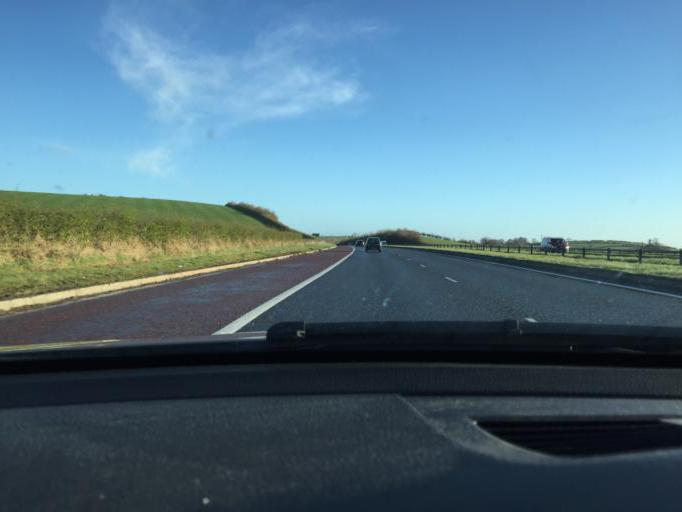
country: GB
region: Northern Ireland
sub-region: Banbridge District
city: Banbridge
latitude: 54.3005
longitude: -6.2972
